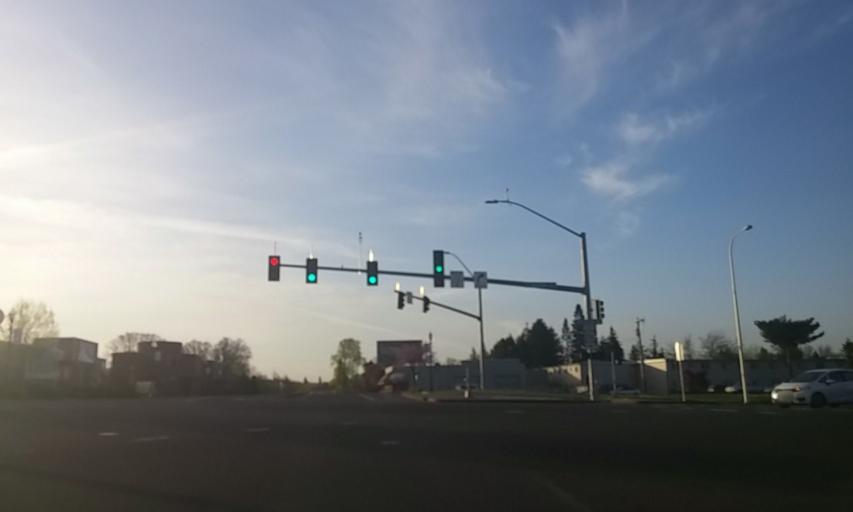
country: US
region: Oregon
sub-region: Washington County
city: Cedar Mill
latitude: 45.5265
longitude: -122.8143
